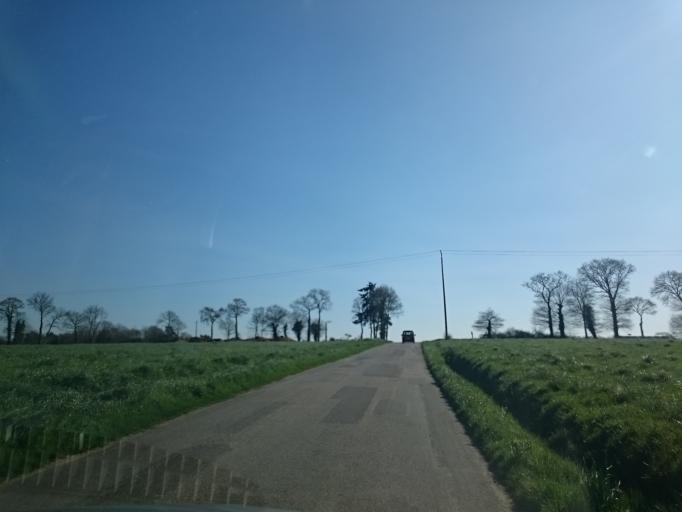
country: FR
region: Brittany
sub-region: Departement d'Ille-et-Vilaine
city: Orgeres
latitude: 47.9851
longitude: -1.6732
